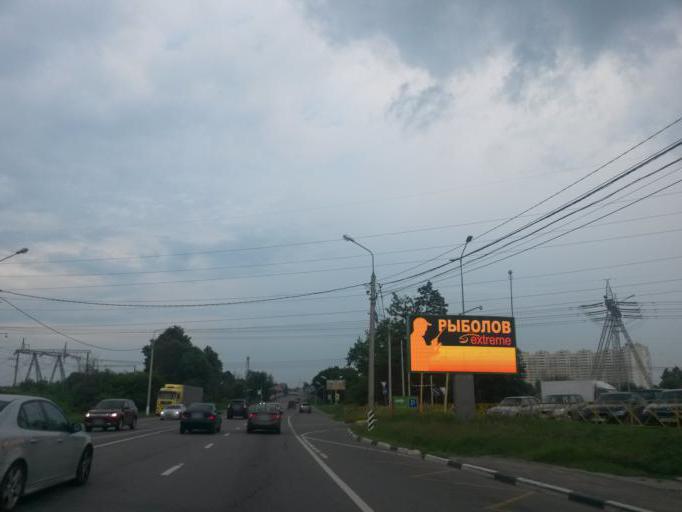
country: RU
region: Moskovskaya
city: Domodedovo
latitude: 55.4596
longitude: 37.7582
